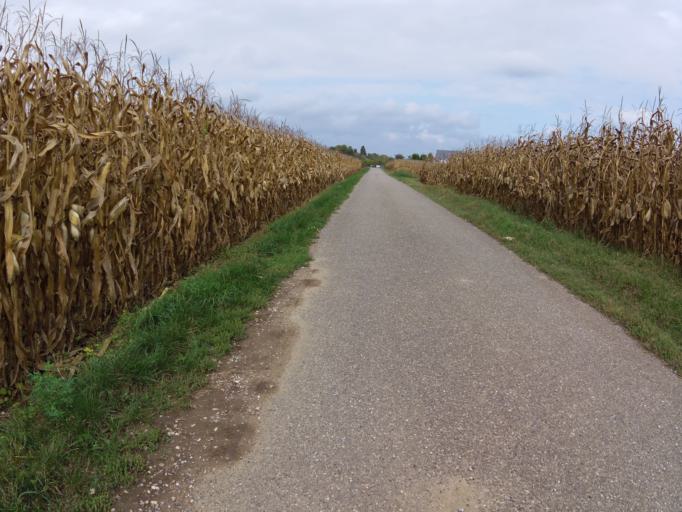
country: FR
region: Alsace
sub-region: Departement du Haut-Rhin
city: Biesheim
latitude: 48.0348
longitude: 7.5397
